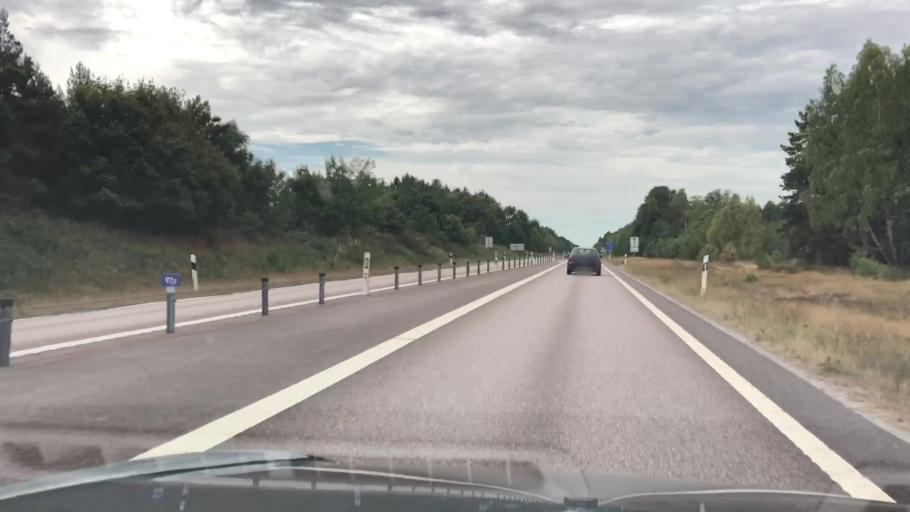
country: SE
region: Blekinge
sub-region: Karlskrona Kommun
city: Jaemjoe
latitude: 56.2130
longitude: 15.8818
